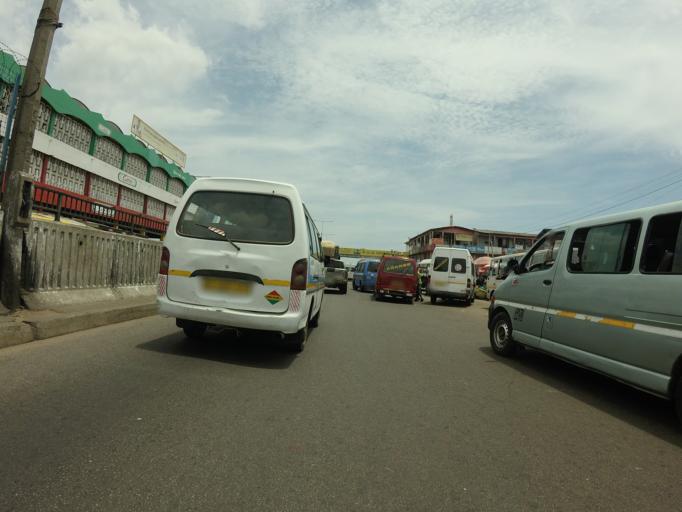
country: GH
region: Greater Accra
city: Accra
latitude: 5.5657
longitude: -0.2367
